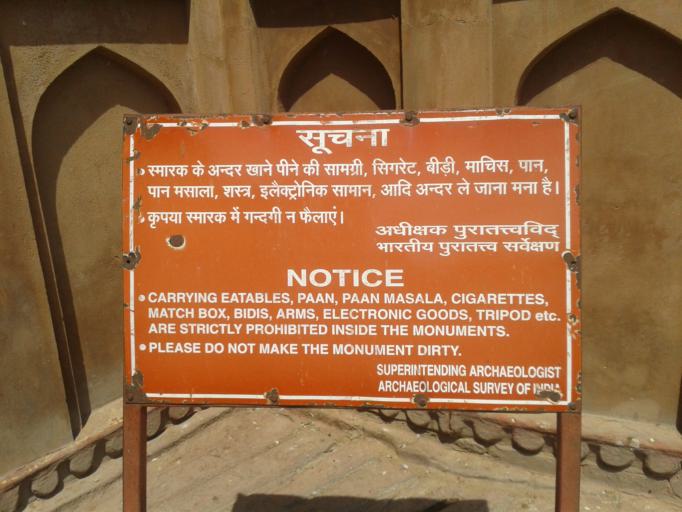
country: IN
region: Uttar Pradesh
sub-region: Agra
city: Agra
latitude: 27.1768
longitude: 78.0225
